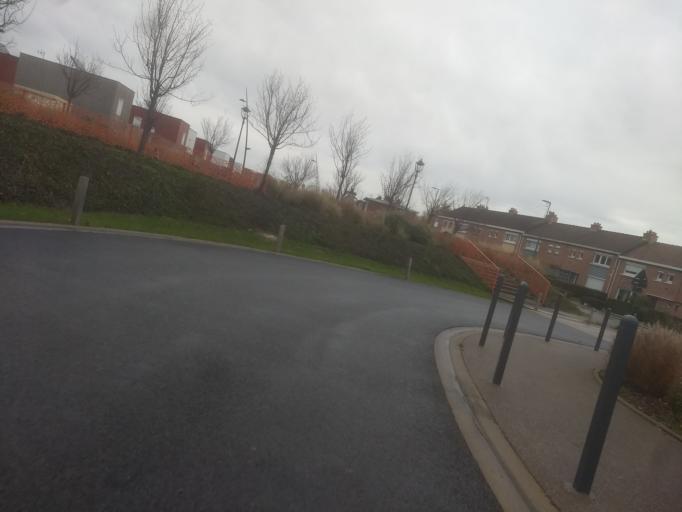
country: FR
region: Nord-Pas-de-Calais
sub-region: Departement du Pas-de-Calais
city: Dainville
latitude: 50.2885
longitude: 2.7374
